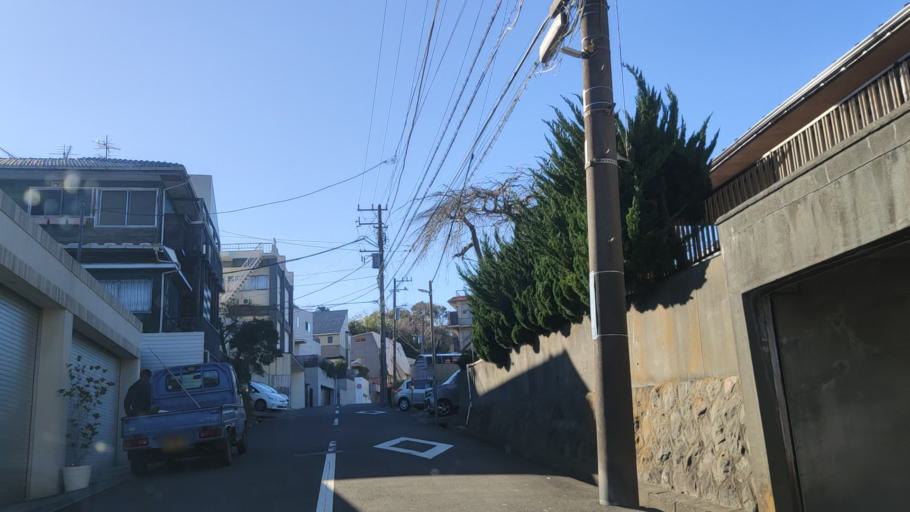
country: JP
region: Kanagawa
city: Yokohama
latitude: 35.4203
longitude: 139.6596
